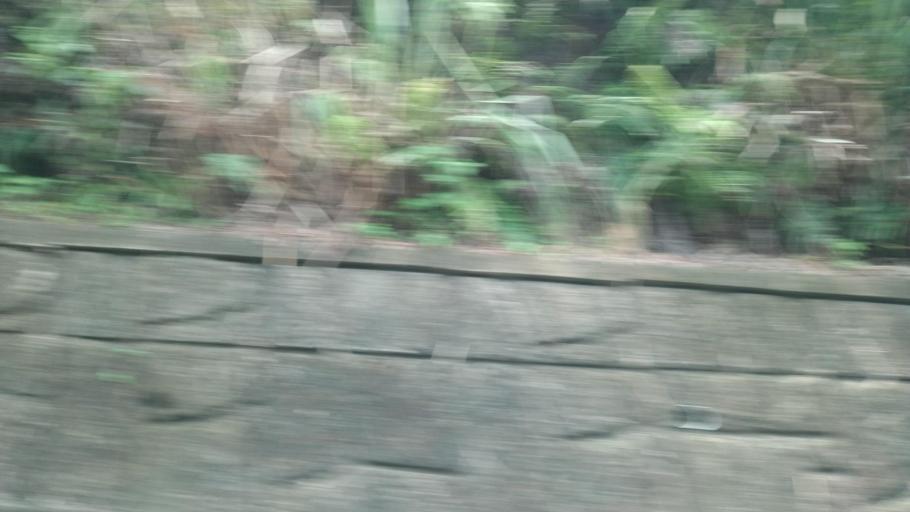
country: TW
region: Taipei
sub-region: Taipei
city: Banqiao
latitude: 24.9354
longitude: 121.4602
